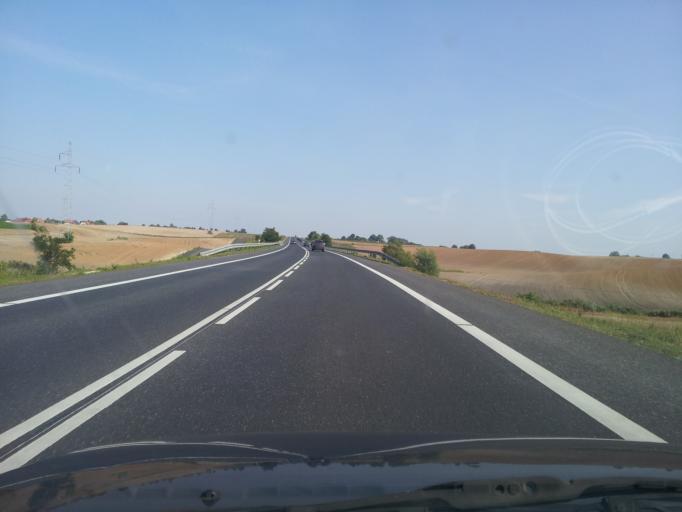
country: PL
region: Greater Poland Voivodeship
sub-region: Powiat gnieznienski
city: Gniezno
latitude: 52.5521
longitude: 17.6431
